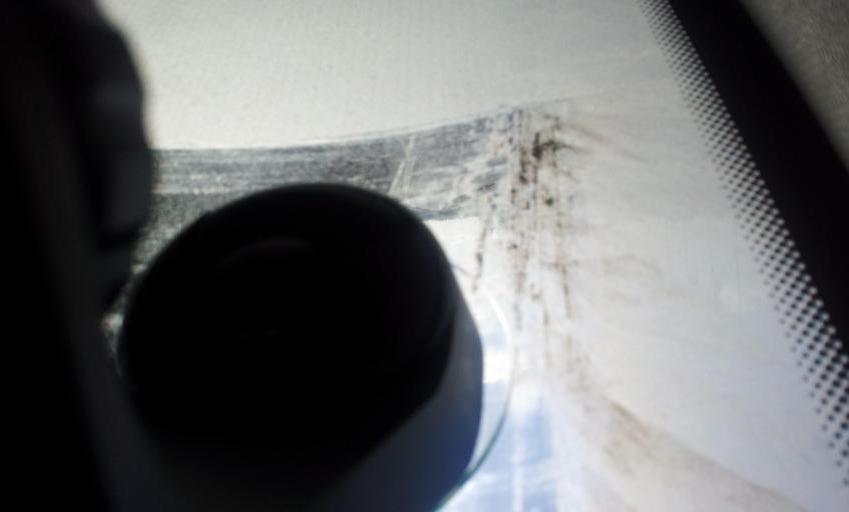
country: SE
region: Kalmar
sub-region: Oskarshamns Kommun
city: Oskarshamn
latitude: 57.3798
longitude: 16.4831
